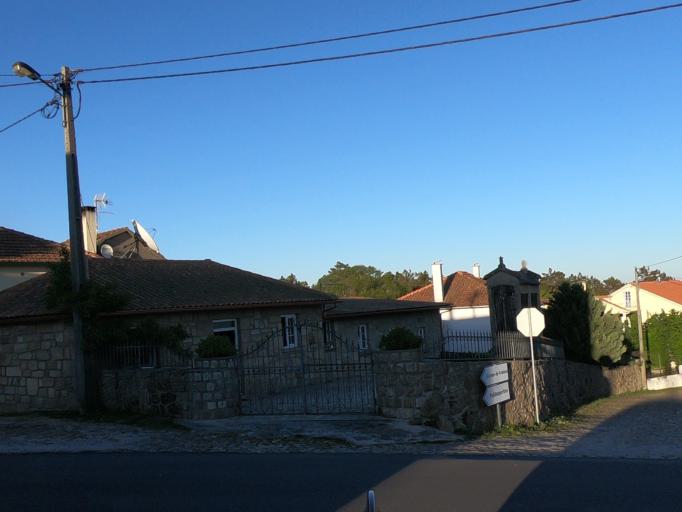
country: PT
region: Vila Real
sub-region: Sabrosa
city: Sabrosa
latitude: 41.3534
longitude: -7.6180
